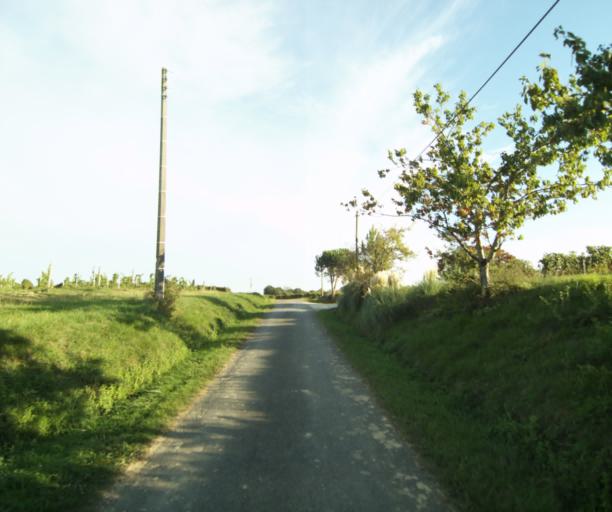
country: FR
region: Midi-Pyrenees
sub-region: Departement du Gers
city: Eauze
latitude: 43.8518
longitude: 0.0138
